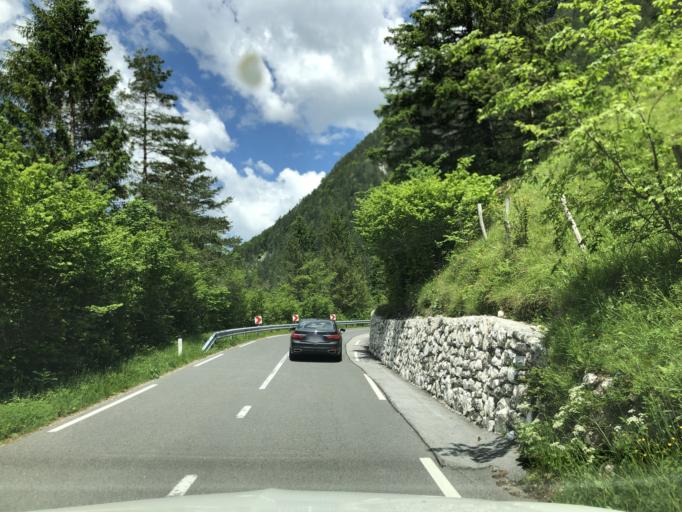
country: SI
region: Bovec
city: Bovec
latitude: 46.3769
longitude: 13.5848
